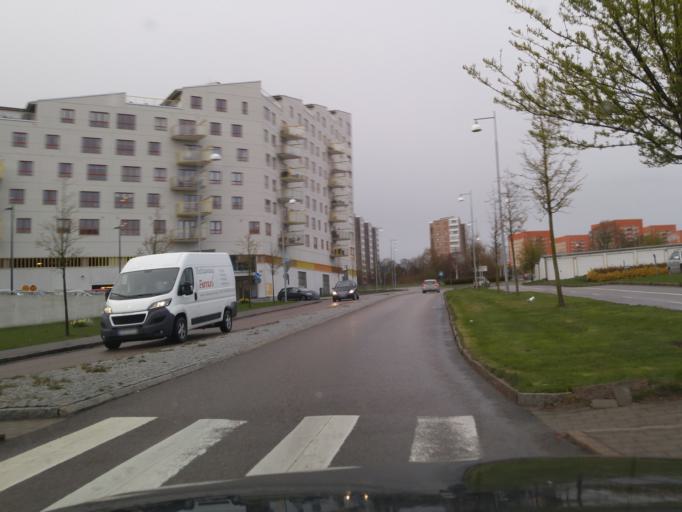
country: SE
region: Vaestra Goetaland
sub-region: Goteborg
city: Majorna
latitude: 57.6531
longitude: 11.9153
